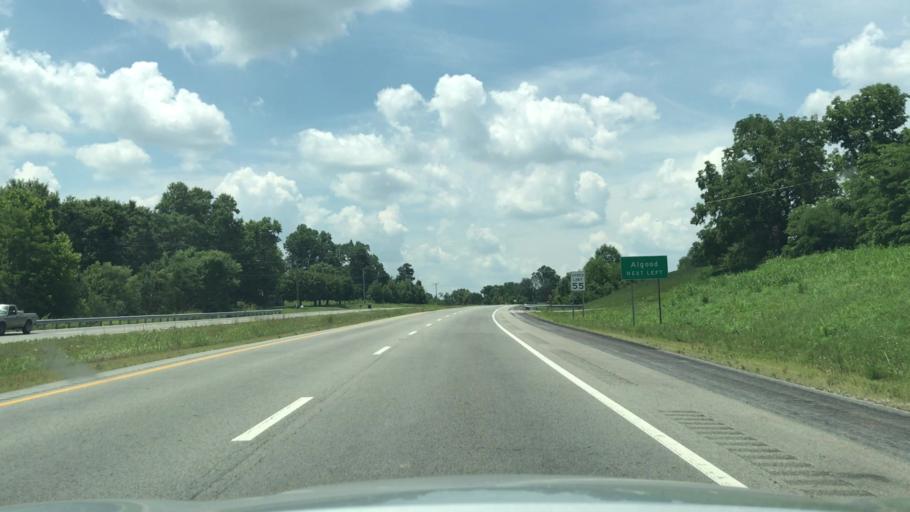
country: US
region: Tennessee
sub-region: Putnam County
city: Algood
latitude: 36.2090
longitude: -85.4309
